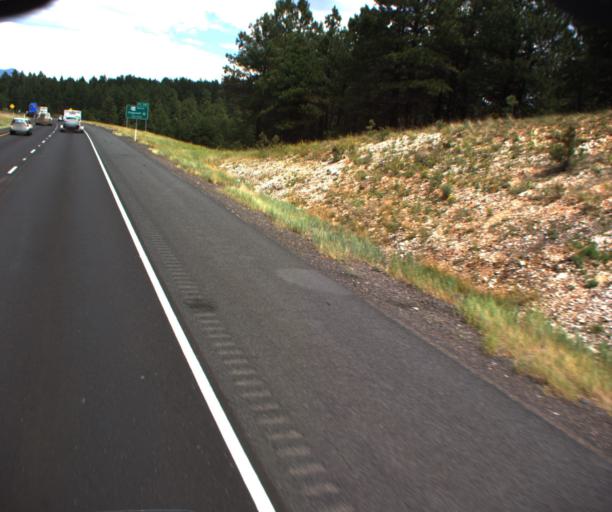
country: US
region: Arizona
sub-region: Coconino County
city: Kachina Village
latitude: 35.1166
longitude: -111.6805
